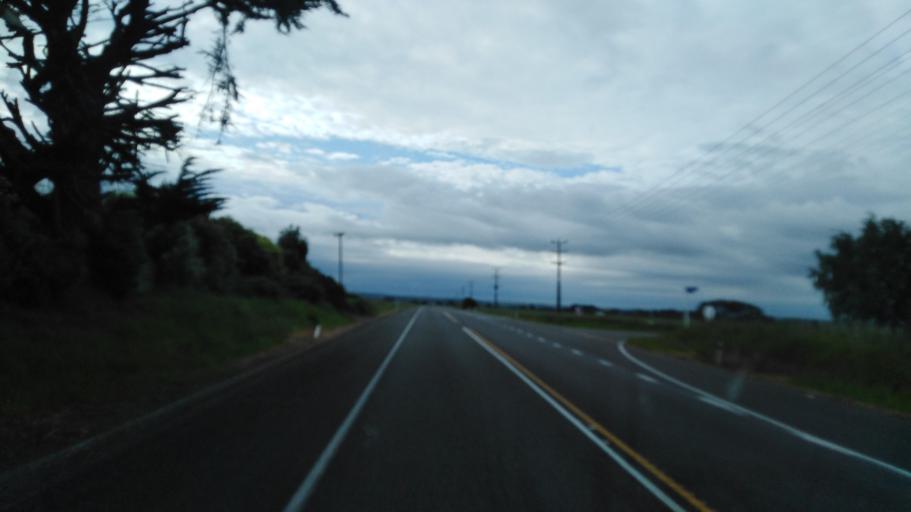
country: NZ
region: Manawatu-Wanganui
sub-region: Rangitikei District
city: Bulls
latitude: -40.1414
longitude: 175.3670
